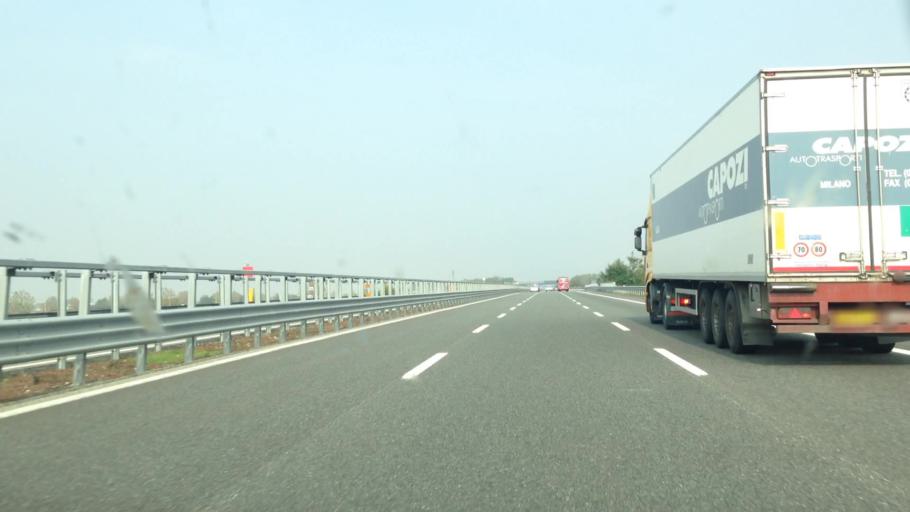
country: IT
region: Piedmont
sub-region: Provincia di Vercelli
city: Caresana
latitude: 45.2186
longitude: 8.4791
